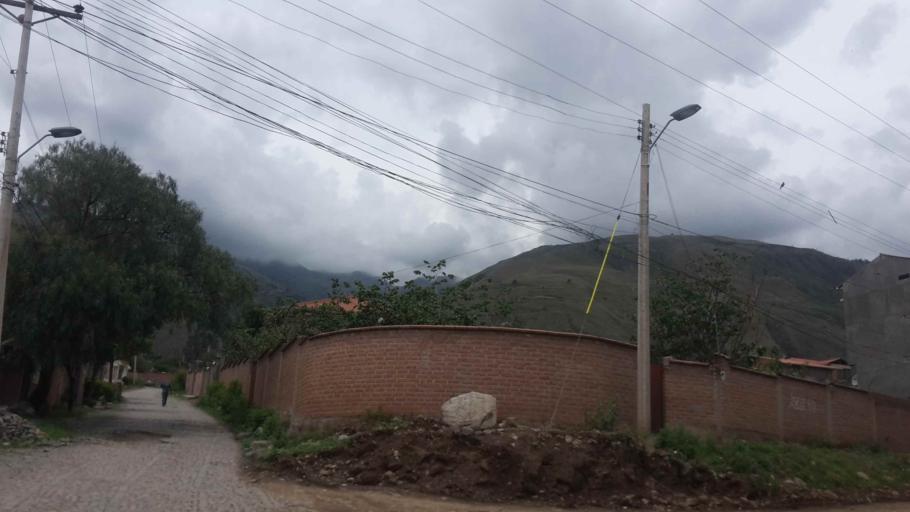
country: BO
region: Cochabamba
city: Cochabamba
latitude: -17.3378
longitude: -66.1876
